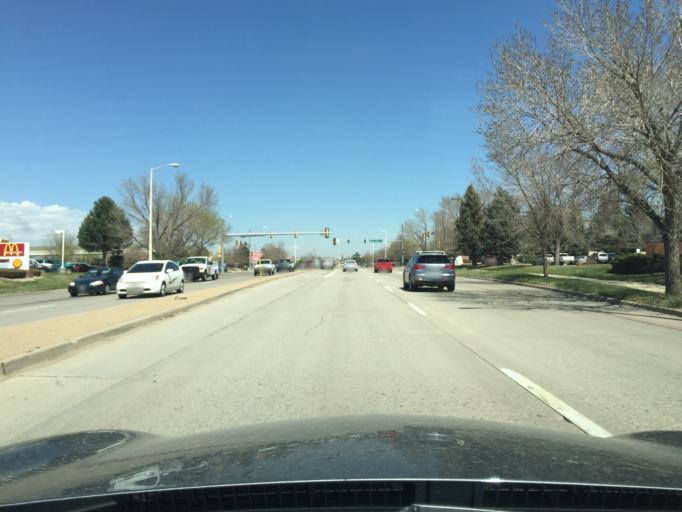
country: US
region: Colorado
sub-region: Boulder County
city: Longmont
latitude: 40.1493
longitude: -105.1307
